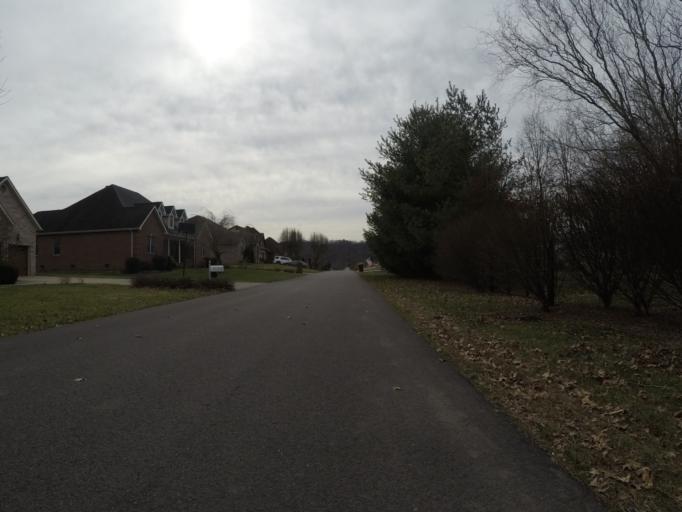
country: US
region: West Virginia
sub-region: Cabell County
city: Pea Ridge
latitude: 38.4491
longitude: -82.3494
